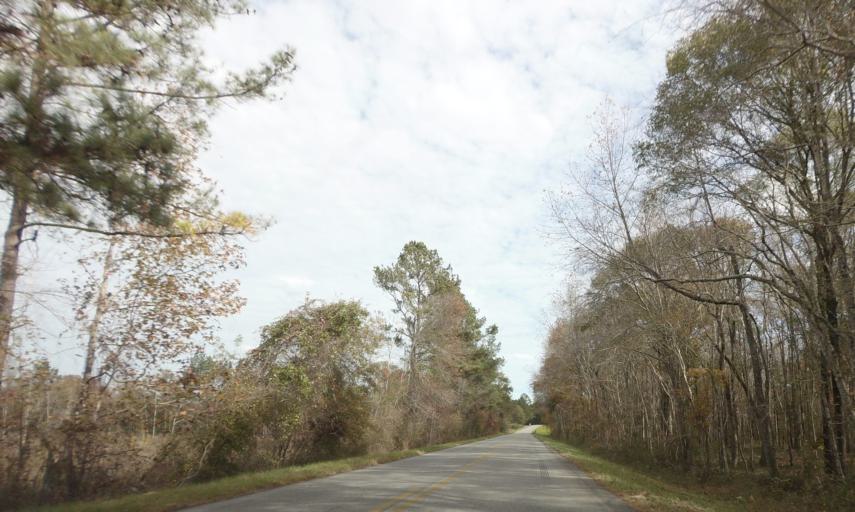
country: US
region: Georgia
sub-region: Dodge County
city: Chester
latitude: 32.4552
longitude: -83.1380
